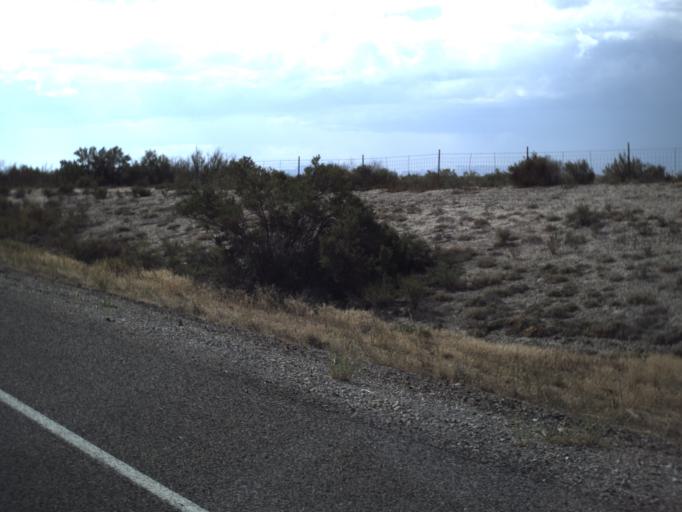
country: US
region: Utah
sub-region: Carbon County
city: East Carbon City
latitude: 38.9911
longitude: -110.1903
